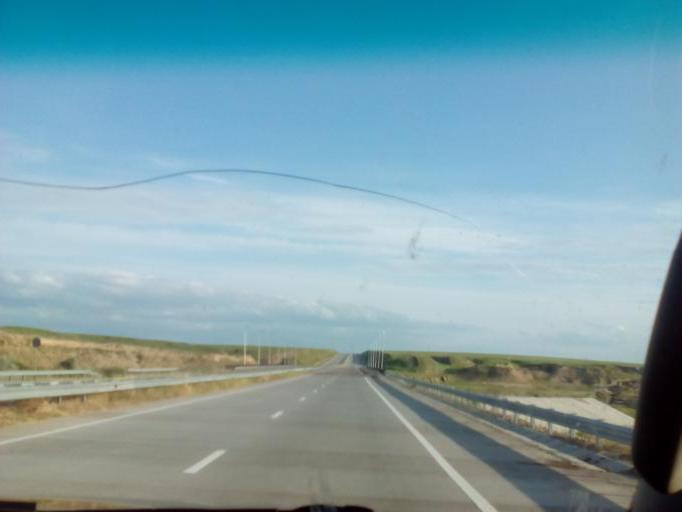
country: KZ
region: Ongtustik Qazaqstan
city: Temirlanovka
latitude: 42.5891
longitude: 69.3089
